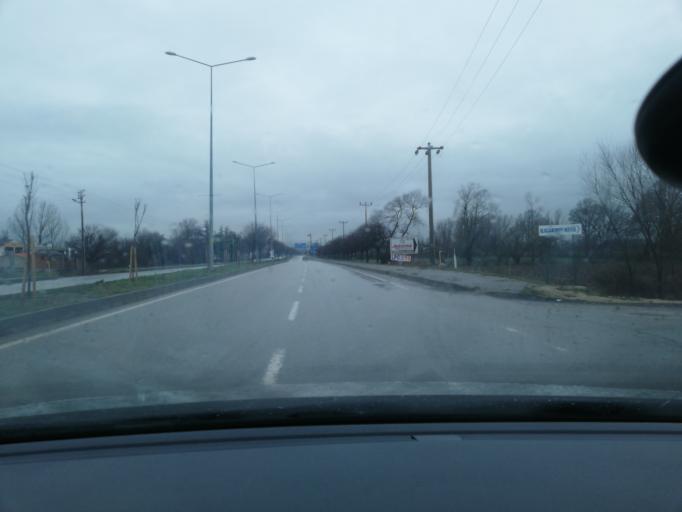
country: TR
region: Bolu
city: Bolu
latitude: 40.6982
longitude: 31.6188
